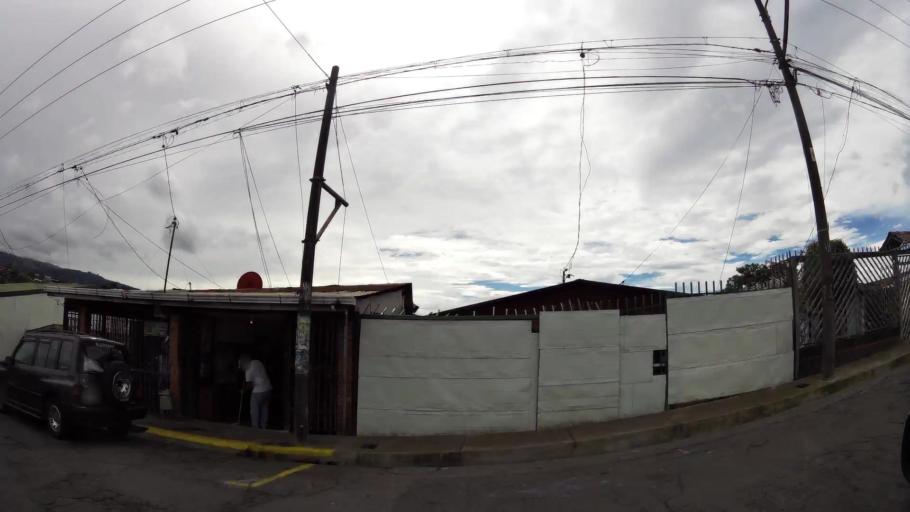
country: CR
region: San Jose
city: Ipis
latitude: 9.9605
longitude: -84.0092
